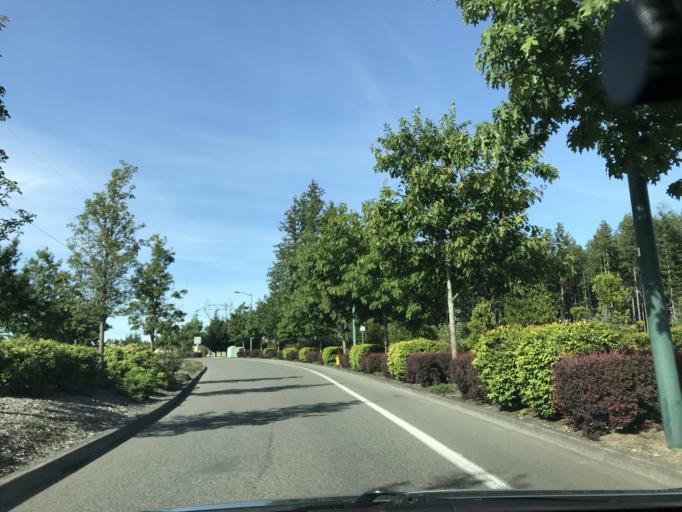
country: US
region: Washington
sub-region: King County
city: Covington
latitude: 47.3554
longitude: -122.1177
